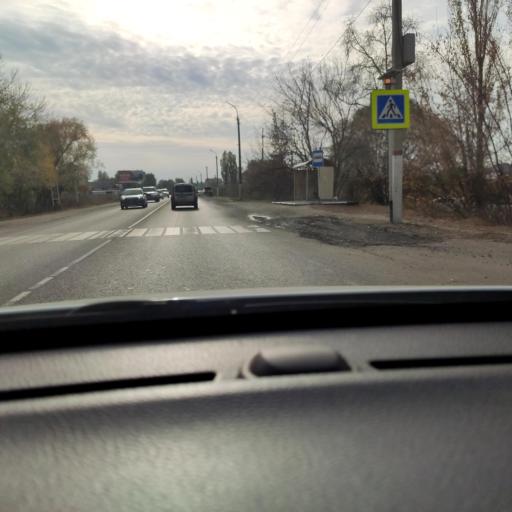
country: RU
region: Voronezj
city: Novaya Usman'
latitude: 51.6226
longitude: 39.3975
